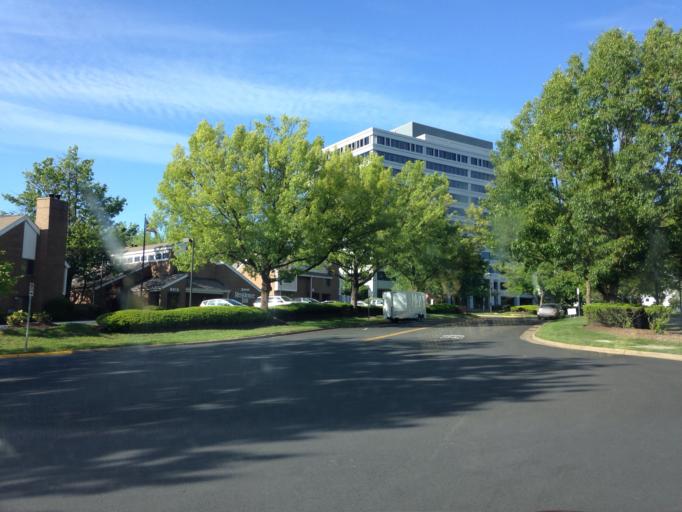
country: US
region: Virginia
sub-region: Fairfax County
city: Tysons Corner
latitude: 38.9286
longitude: -77.2483
